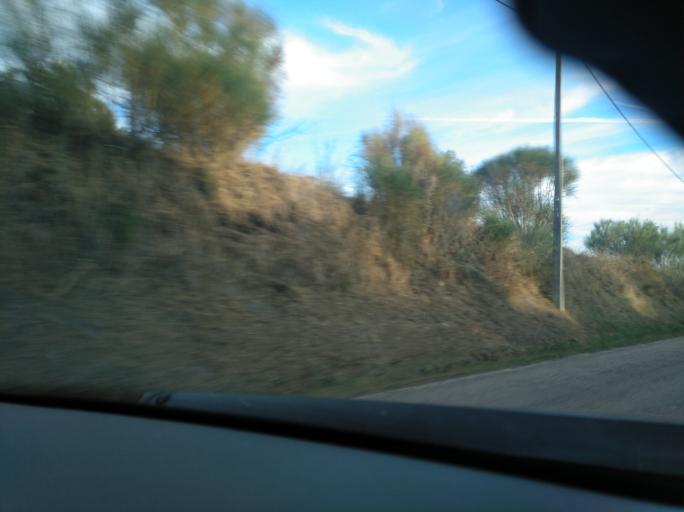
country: PT
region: Evora
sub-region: Arraiolos
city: Arraiolos
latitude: 38.8435
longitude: -7.8293
